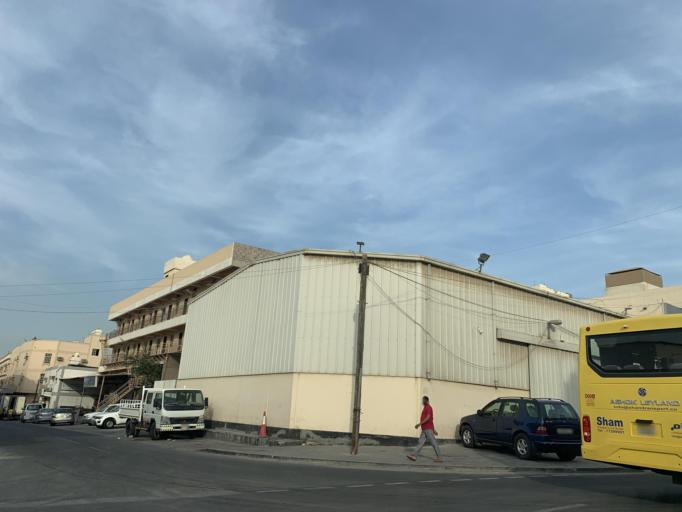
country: BH
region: Northern
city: Ar Rifa'
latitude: 26.1237
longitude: 50.5854
